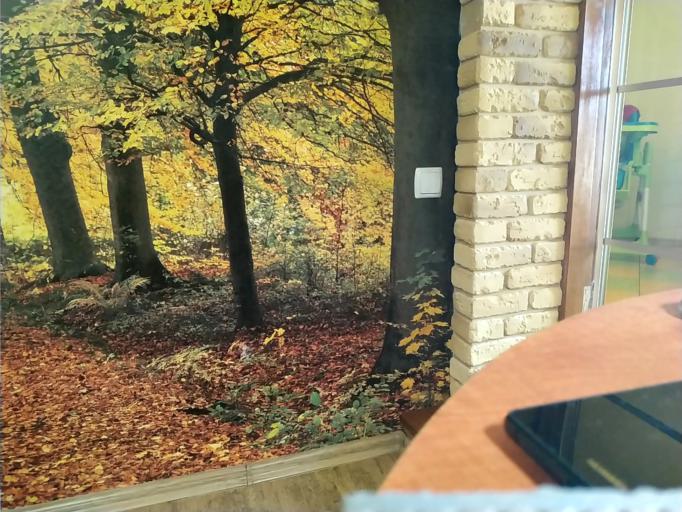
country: RU
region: Kaluga
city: Kondrovo
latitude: 54.8259
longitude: 35.9467
